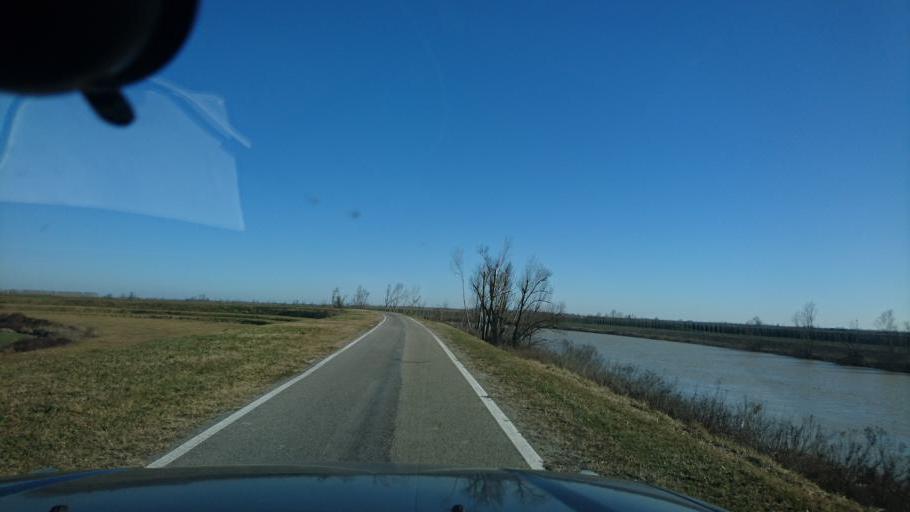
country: IT
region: Veneto
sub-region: Provincia di Rovigo
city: Ariano
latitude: 44.9316
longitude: 12.1548
